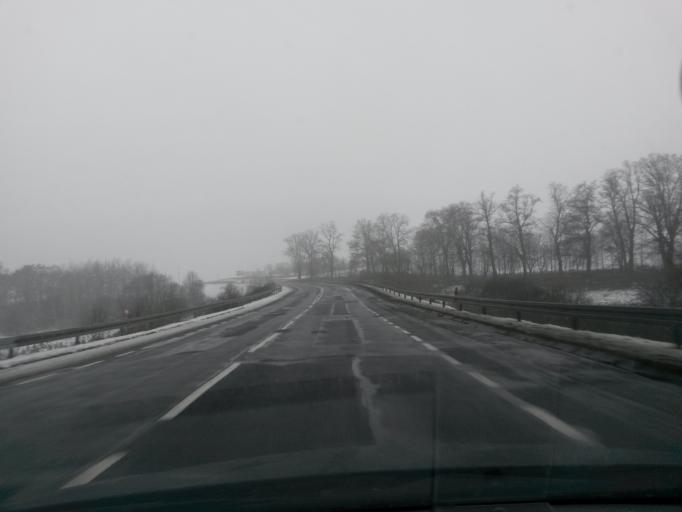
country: PL
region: Kujawsko-Pomorskie
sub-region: Powiat nakielski
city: Slesin
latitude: 53.1687
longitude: 17.6820
